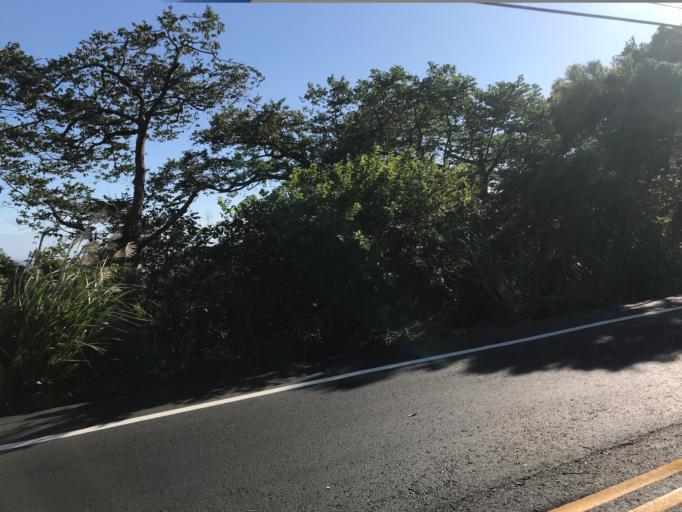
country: TW
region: Taiwan
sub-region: Hsinchu
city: Zhubei
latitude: 24.8686
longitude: 121.0930
